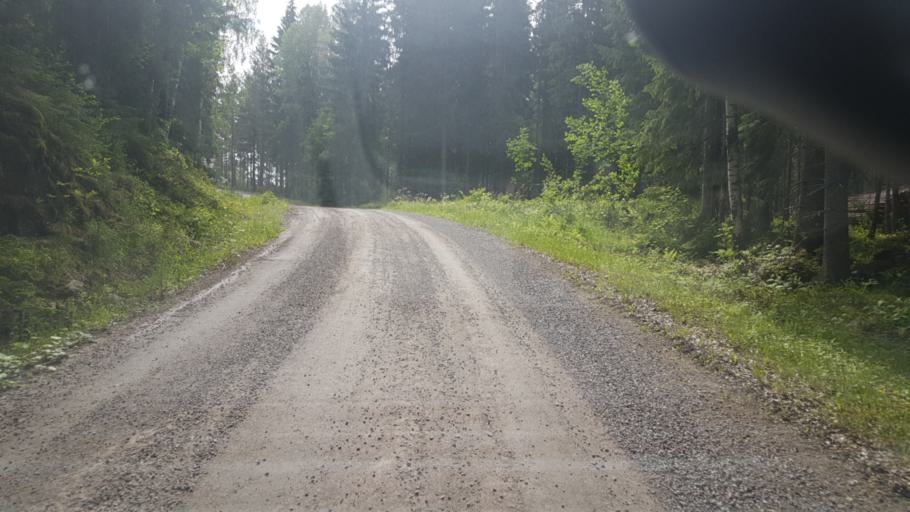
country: SE
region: Vaermland
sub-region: Eda Kommun
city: Amotfors
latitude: 59.8011
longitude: 12.4418
